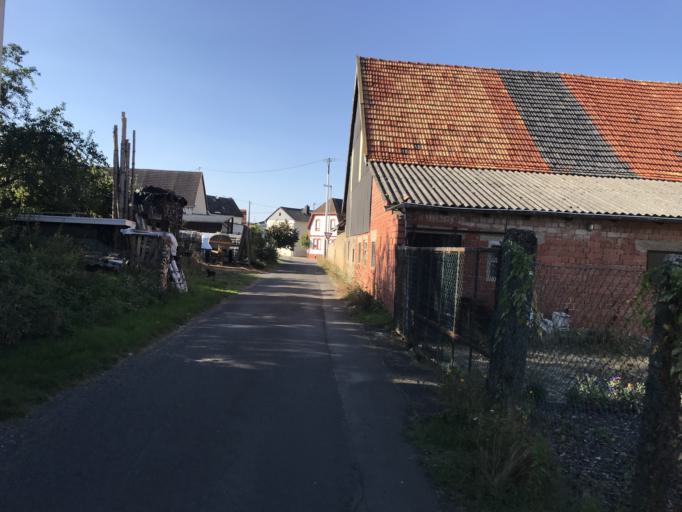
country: DE
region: Hesse
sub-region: Regierungsbezirk Darmstadt
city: Altenstadt
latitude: 50.2698
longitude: 8.9281
